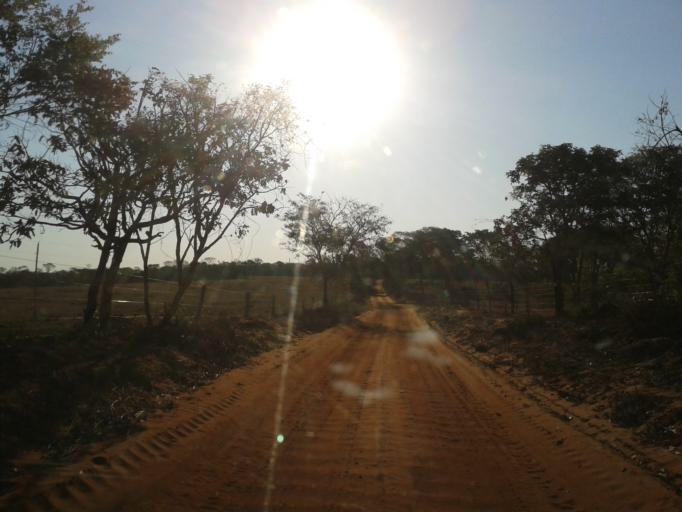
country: BR
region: Minas Gerais
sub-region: Campina Verde
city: Campina Verde
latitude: -19.2542
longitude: -49.5745
